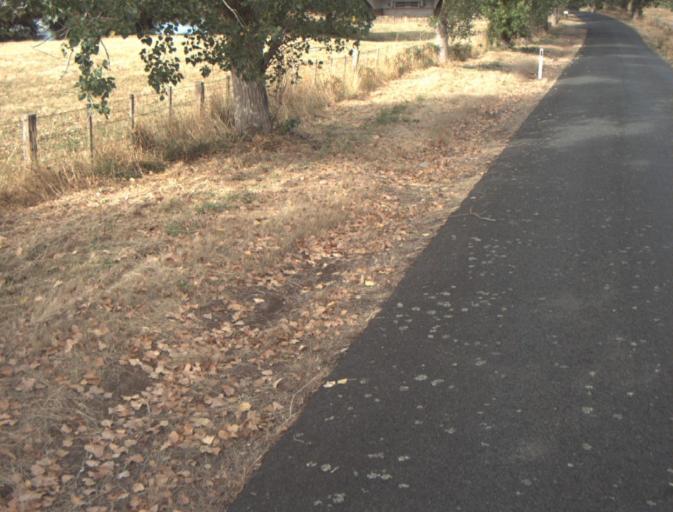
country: AU
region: Tasmania
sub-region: Launceston
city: Mayfield
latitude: -41.2865
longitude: 147.2136
